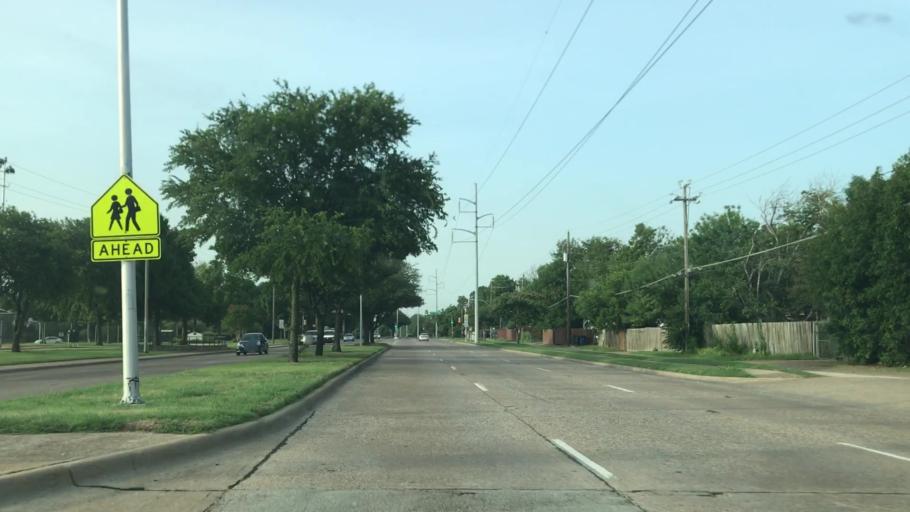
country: US
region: Texas
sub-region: Dallas County
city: Balch Springs
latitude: 32.7871
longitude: -96.7002
